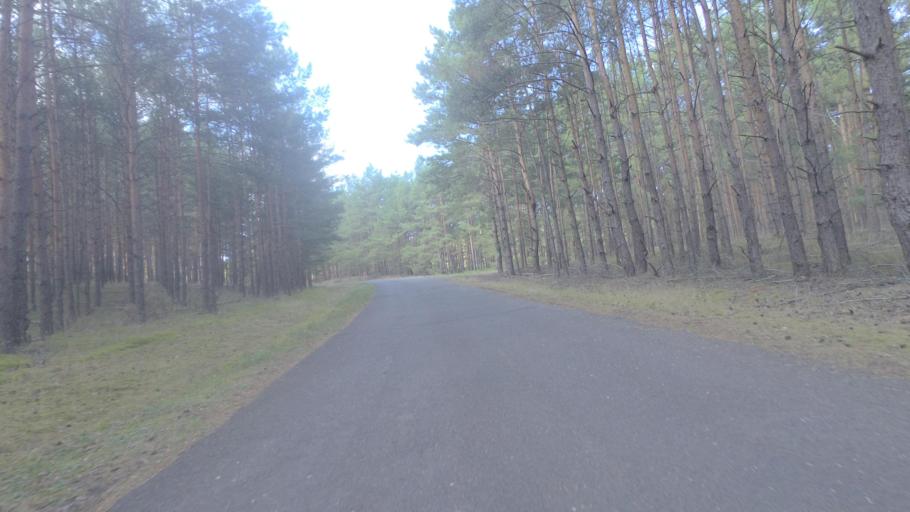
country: DE
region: Brandenburg
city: Munchehofe
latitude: 52.1720
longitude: 13.8808
